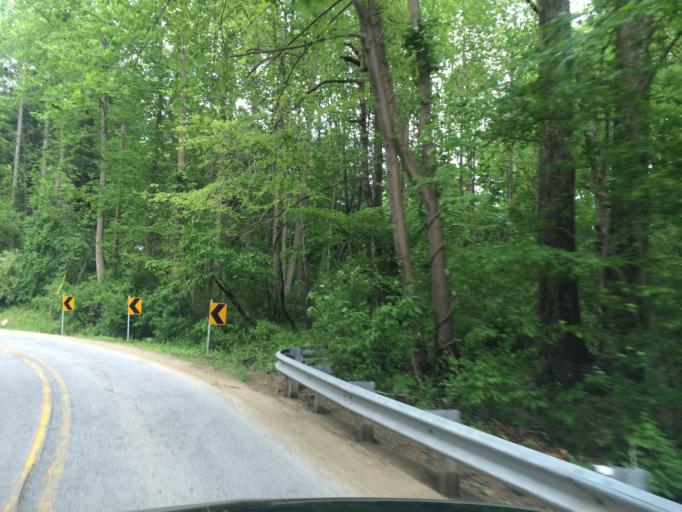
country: US
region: Maryland
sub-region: Howard County
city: Riverside
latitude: 39.2000
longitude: -76.9192
